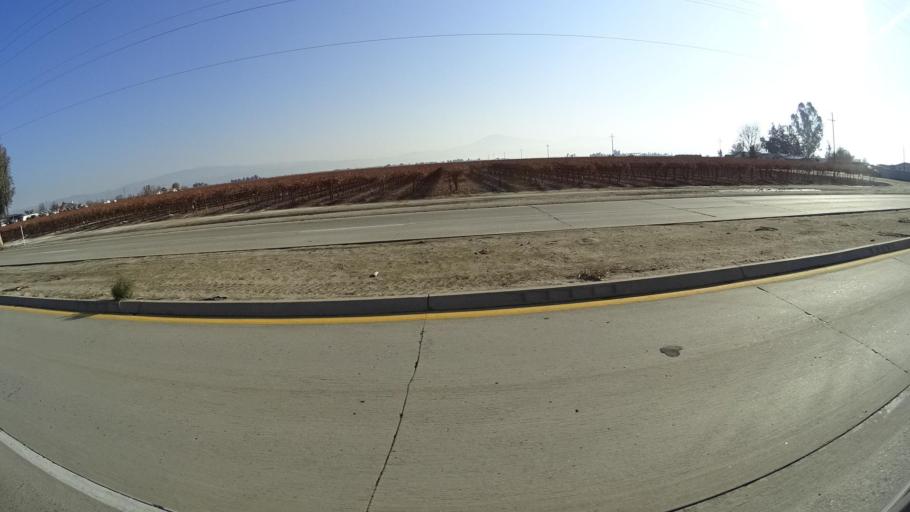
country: US
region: California
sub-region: Kern County
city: Greenfield
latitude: 35.2422
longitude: -119.0032
